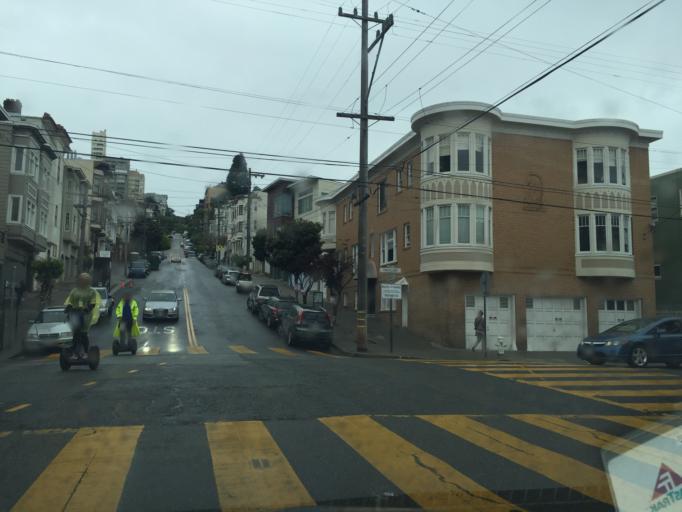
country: US
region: California
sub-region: San Francisco County
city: San Francisco
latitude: 37.8026
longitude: -122.4145
